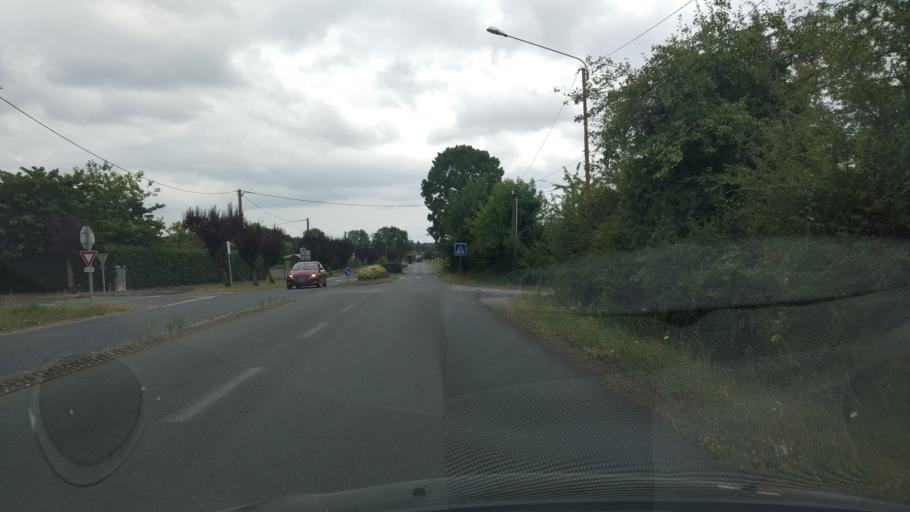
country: FR
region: Poitou-Charentes
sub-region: Departement de la Vienne
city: Roches-Premarie-Andille
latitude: 46.4898
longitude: 0.3679
